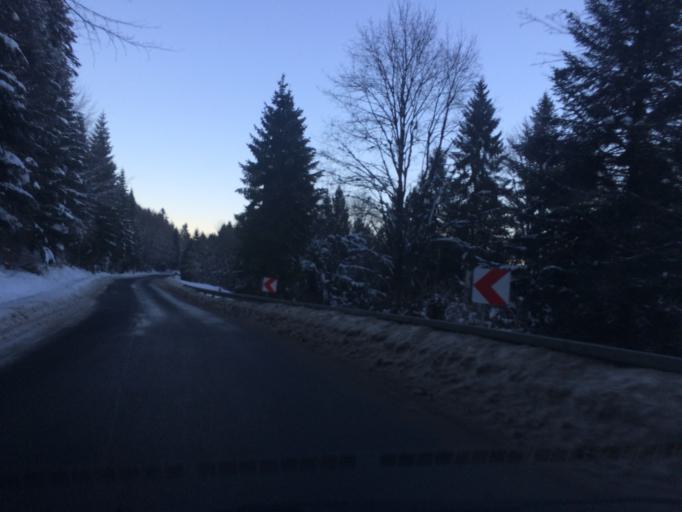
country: PL
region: Subcarpathian Voivodeship
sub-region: Powiat bieszczadzki
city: Lutowiska
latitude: 49.2813
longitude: 22.6840
